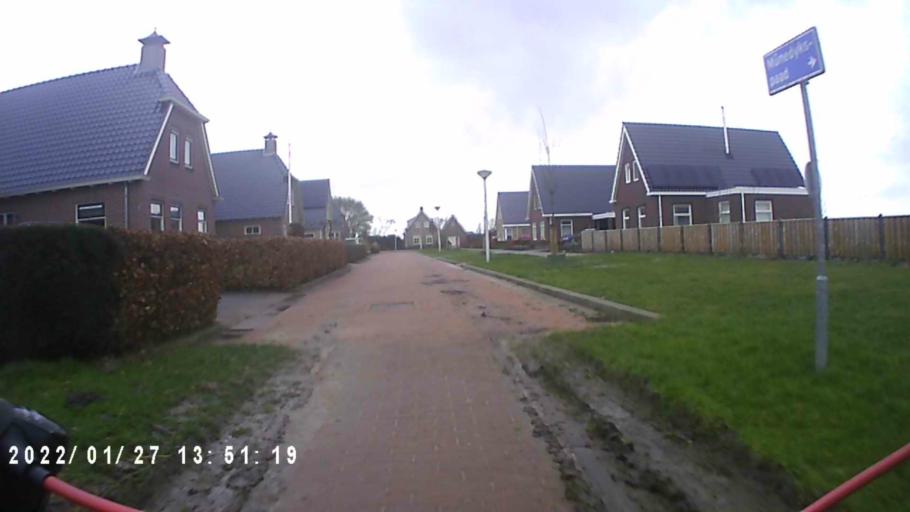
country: NL
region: Friesland
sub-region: Gemeente Kollumerland en Nieuwkruisland
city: Kollum
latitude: 53.3060
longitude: 6.1913
